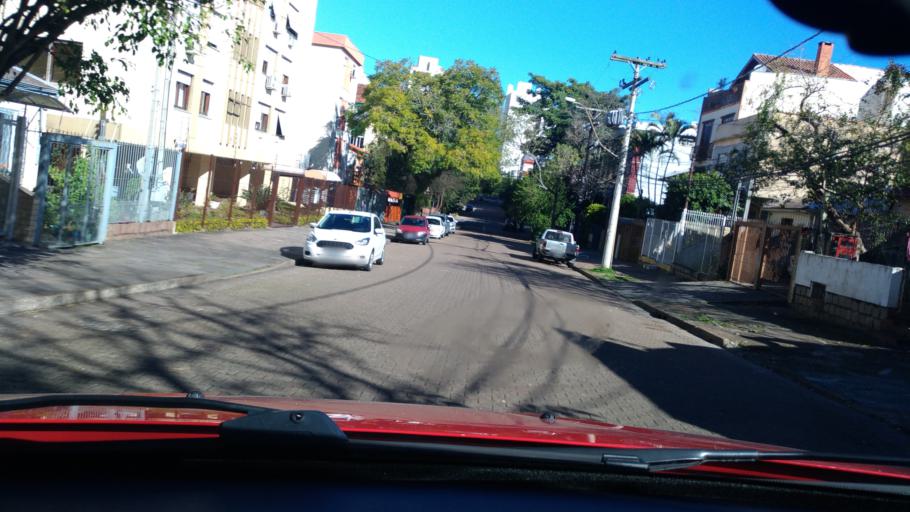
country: BR
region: Rio Grande do Sul
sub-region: Porto Alegre
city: Porto Alegre
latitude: -30.0092
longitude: -51.1639
